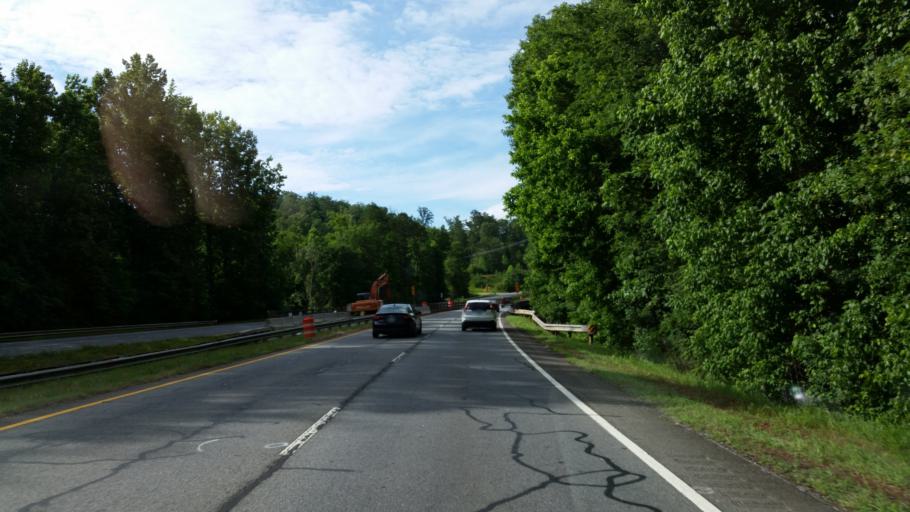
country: US
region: Georgia
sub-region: Bartow County
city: Emerson
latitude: 34.1100
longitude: -84.7498
